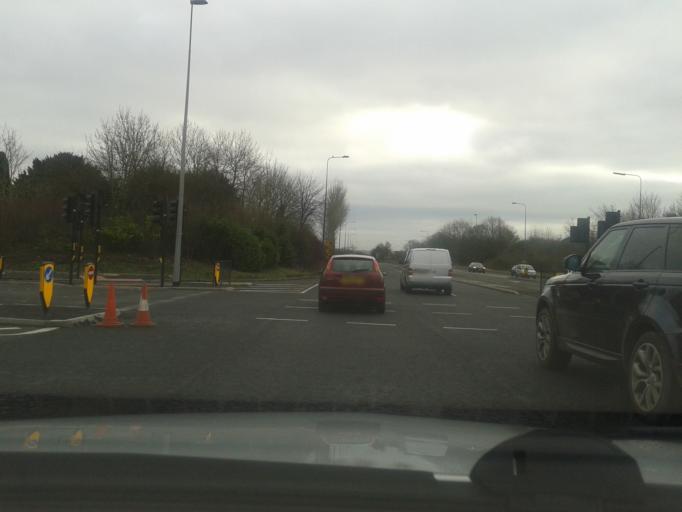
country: GB
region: England
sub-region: South Gloucestershire
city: Stoke Gifford
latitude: 51.5042
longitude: -2.5210
